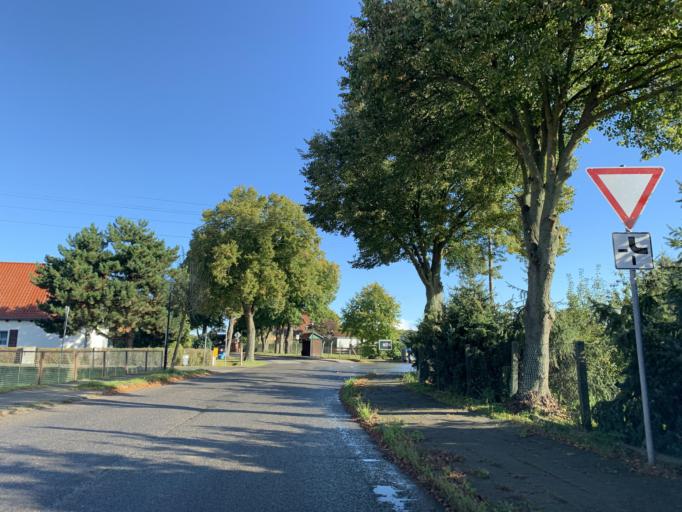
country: DE
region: Mecklenburg-Vorpommern
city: Burg Stargard
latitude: 53.4862
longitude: 13.2703
